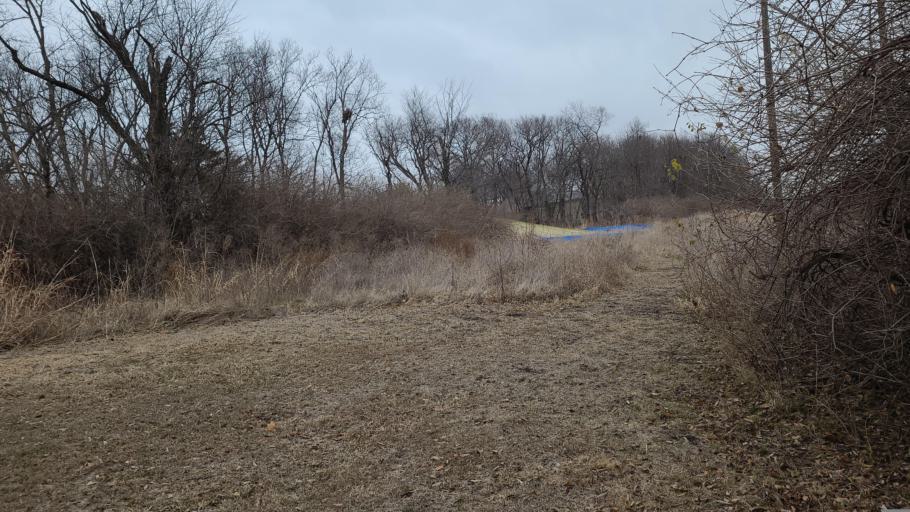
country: US
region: Kansas
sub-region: Douglas County
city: Lawrence
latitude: 38.9789
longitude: -95.2825
